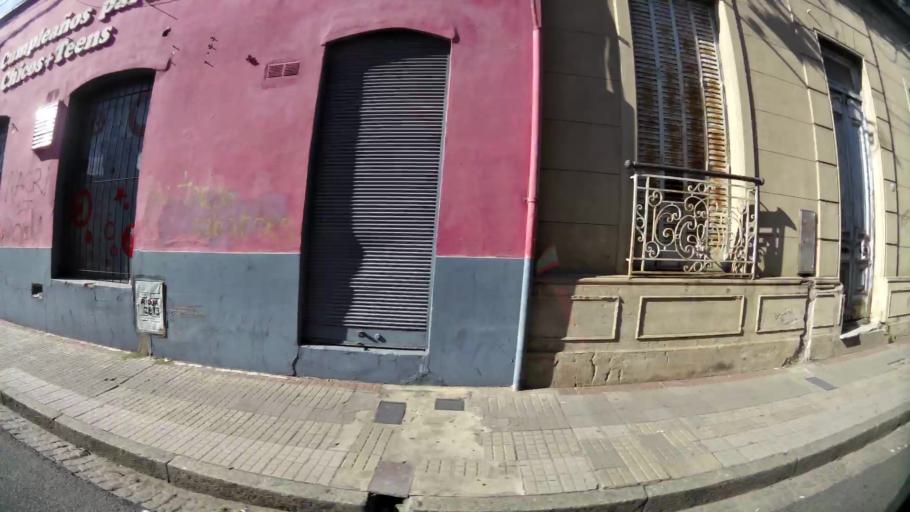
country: AR
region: Santa Fe
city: Santa Fe de la Vera Cruz
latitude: -31.6450
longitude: -60.7091
